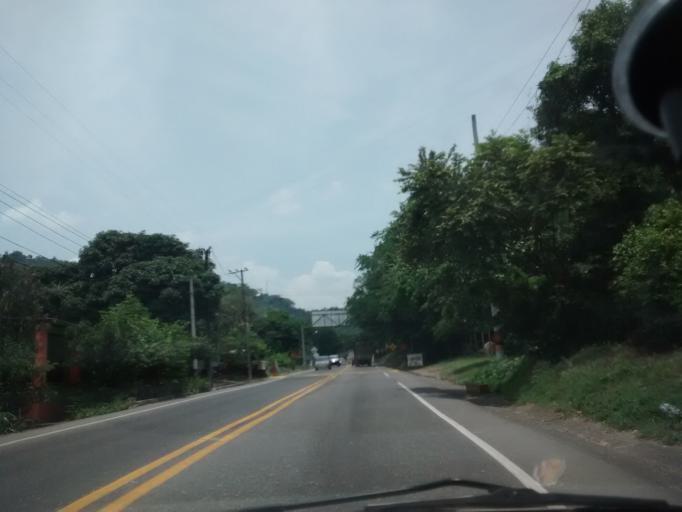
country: CO
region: Tolima
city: Valle de San Juan
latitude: 4.2854
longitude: -75.0331
